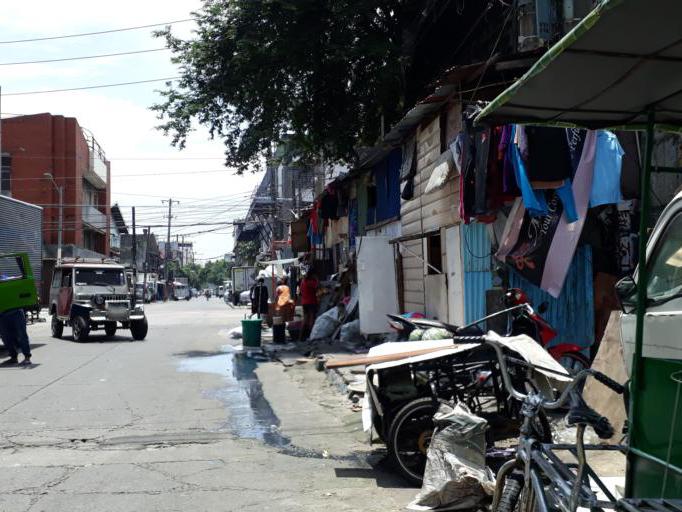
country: PH
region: Metro Manila
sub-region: Caloocan City
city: Niugan
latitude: 14.6480
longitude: 120.9807
